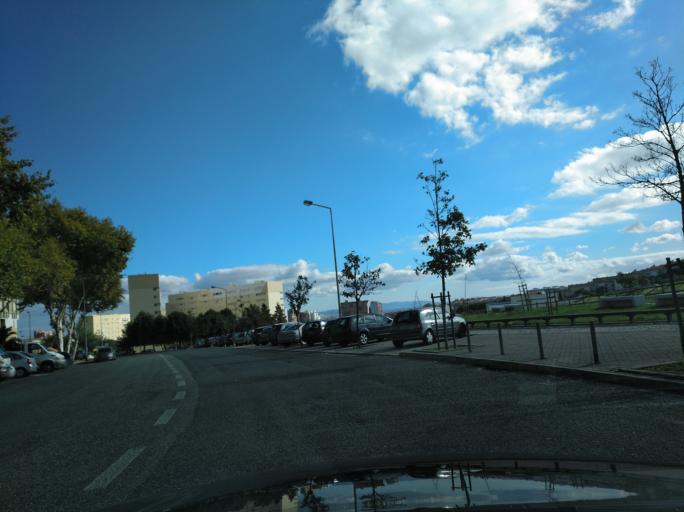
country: PT
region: Lisbon
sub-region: Loures
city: Moscavide
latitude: 38.7576
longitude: -9.1230
